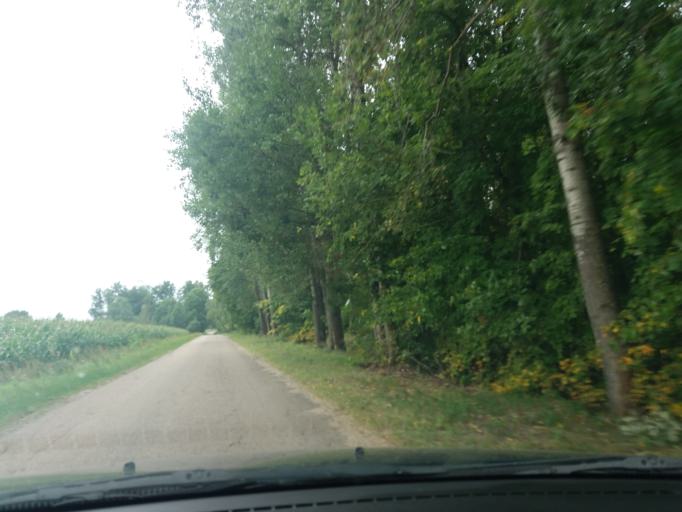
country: PL
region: Masovian Voivodeship
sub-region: Powiat mlawski
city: Wieczfnia Koscielna
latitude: 53.2323
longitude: 20.4900
